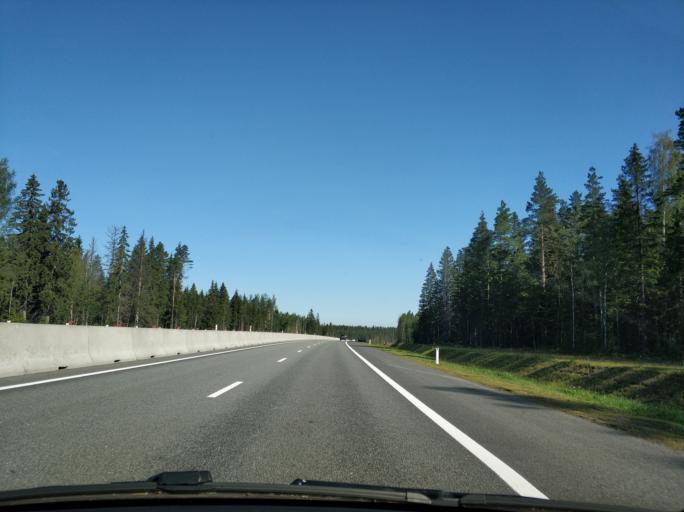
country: RU
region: Leningrad
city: Sosnovo
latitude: 60.5245
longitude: 30.1684
